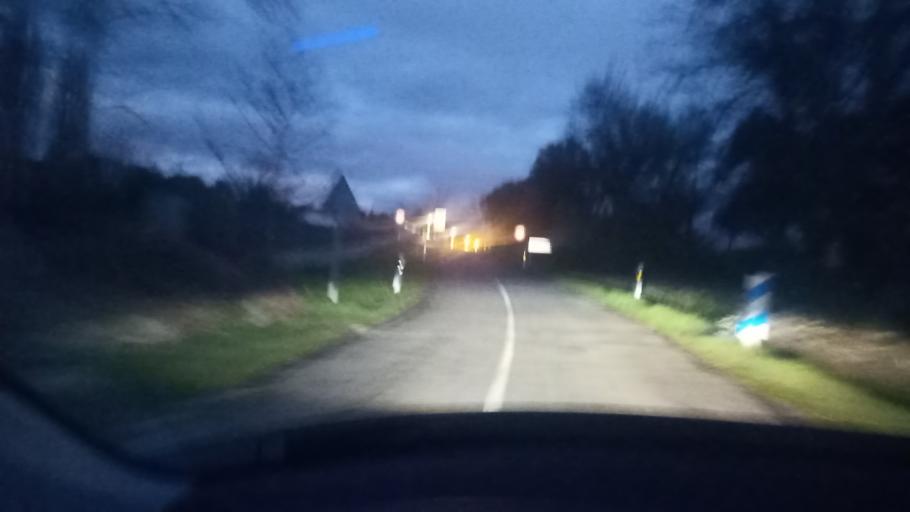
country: ES
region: Madrid
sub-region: Provincia de Madrid
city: Colmenar del Arroyo
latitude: 40.4239
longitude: -4.2020
